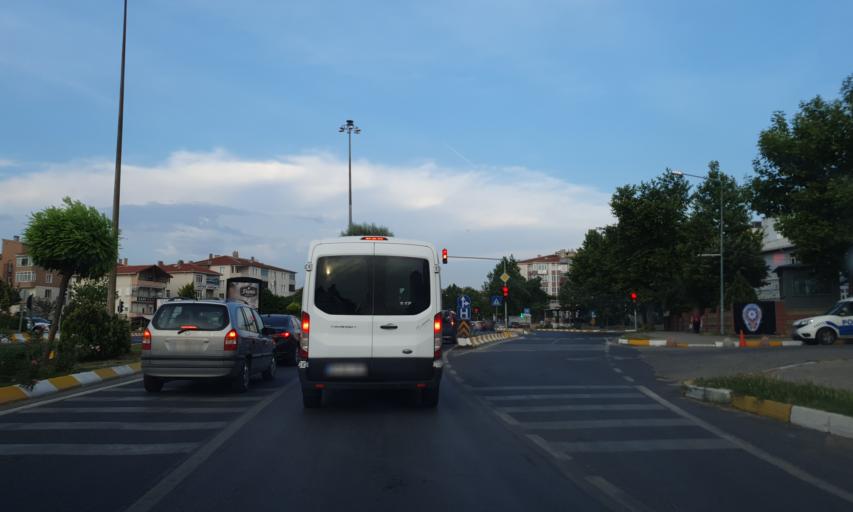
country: TR
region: Kirklareli
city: Luleburgaz
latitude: 41.4026
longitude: 27.3647
